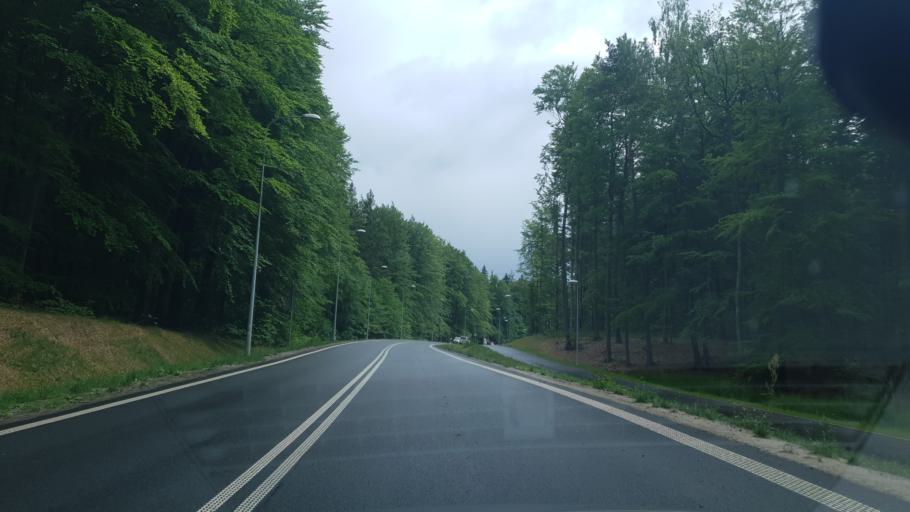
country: PL
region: Pomeranian Voivodeship
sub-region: Powiat kartuski
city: Kartuzy
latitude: 54.3429
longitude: 18.2139
